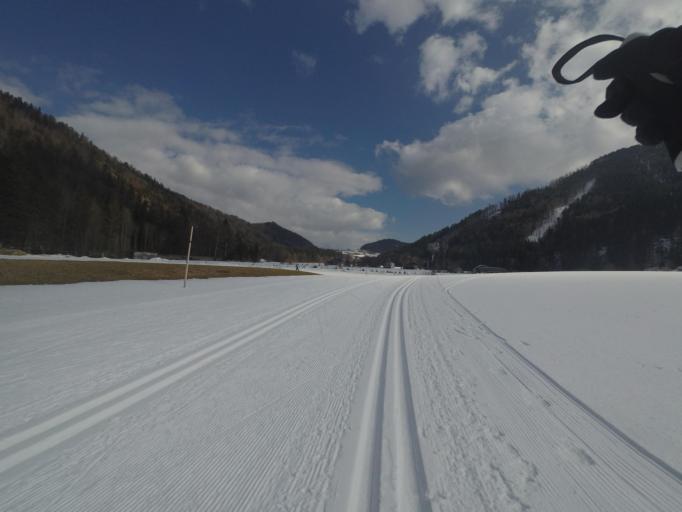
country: AT
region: Salzburg
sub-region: Politischer Bezirk Salzburg-Umgebung
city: Fuschl am See
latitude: 47.7667
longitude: 13.3203
